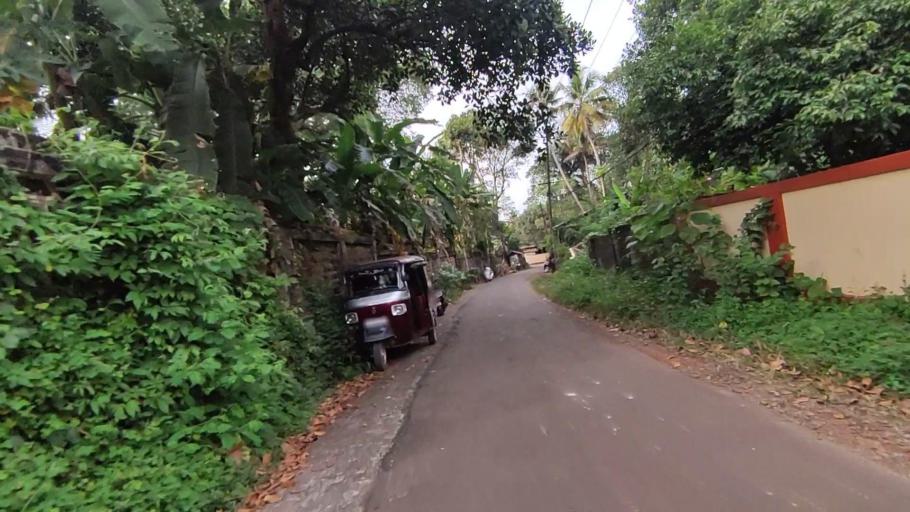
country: IN
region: Kerala
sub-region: Kottayam
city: Kottayam
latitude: 9.6101
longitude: 76.4849
